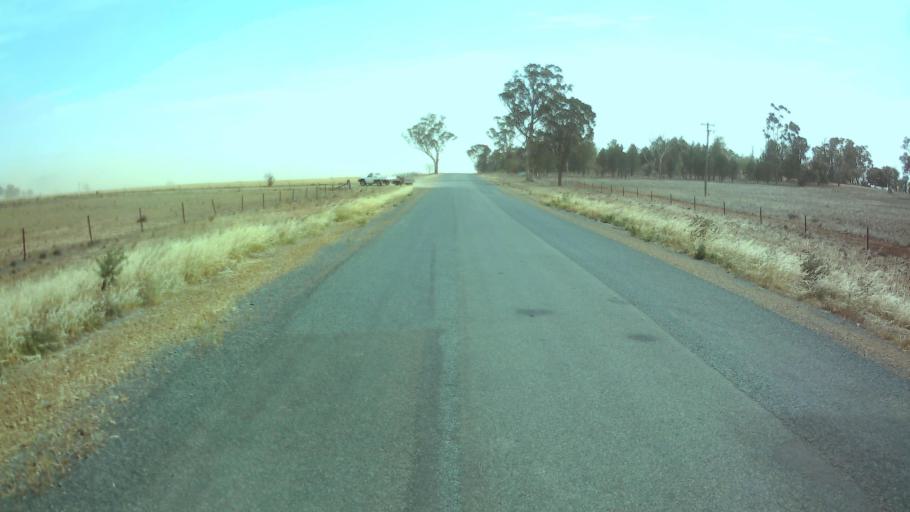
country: AU
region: New South Wales
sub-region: Weddin
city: Grenfell
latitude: -33.7486
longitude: 147.9912
